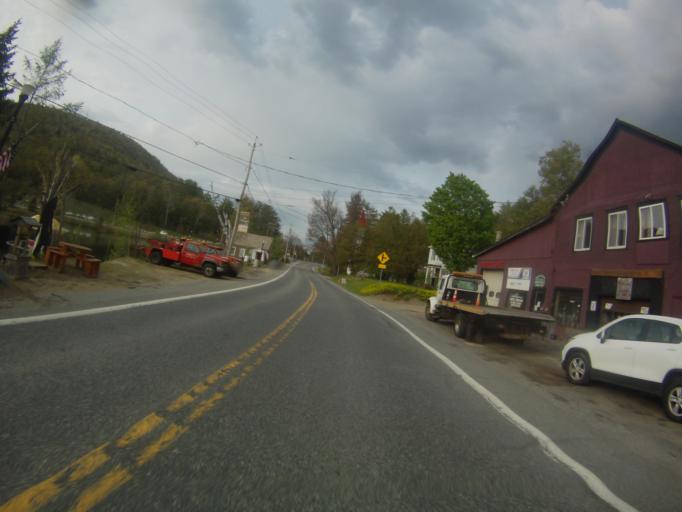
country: US
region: New York
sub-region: Warren County
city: Warrensburg
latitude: 43.6762
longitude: -73.7501
